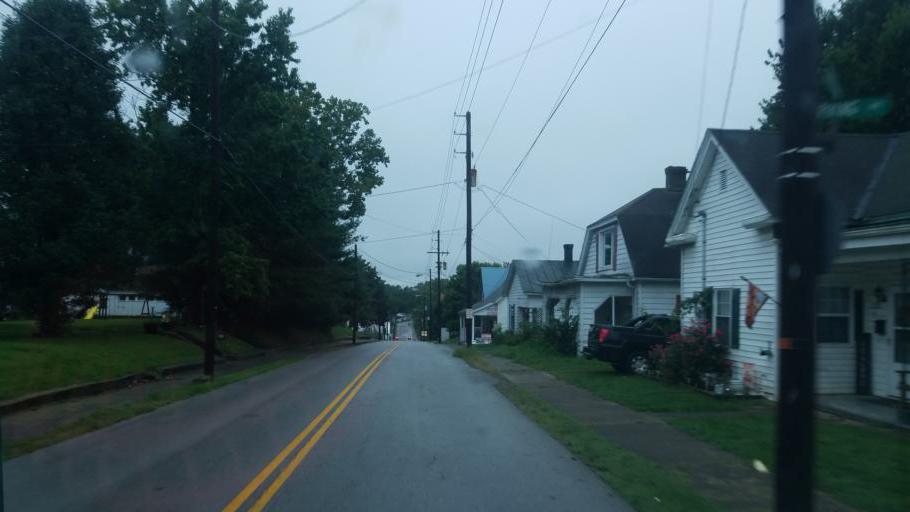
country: US
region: Kentucky
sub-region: Fleming County
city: Flemingsburg
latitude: 38.4225
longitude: -83.7302
